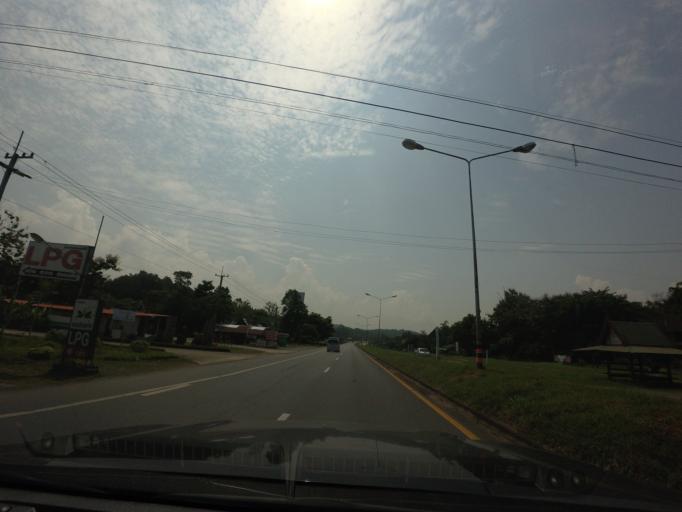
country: TH
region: Phrae
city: Den Chai
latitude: 17.9580
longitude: 100.0677
